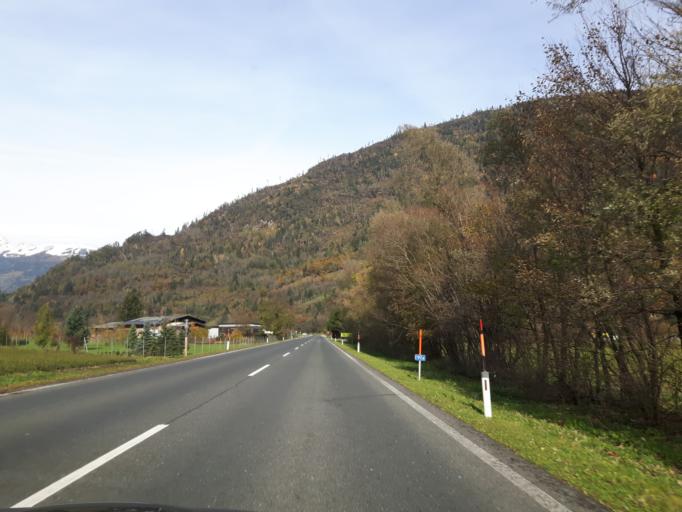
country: AT
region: Tyrol
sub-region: Politischer Bezirk Lienz
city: Lavant
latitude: 46.7946
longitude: 12.8749
